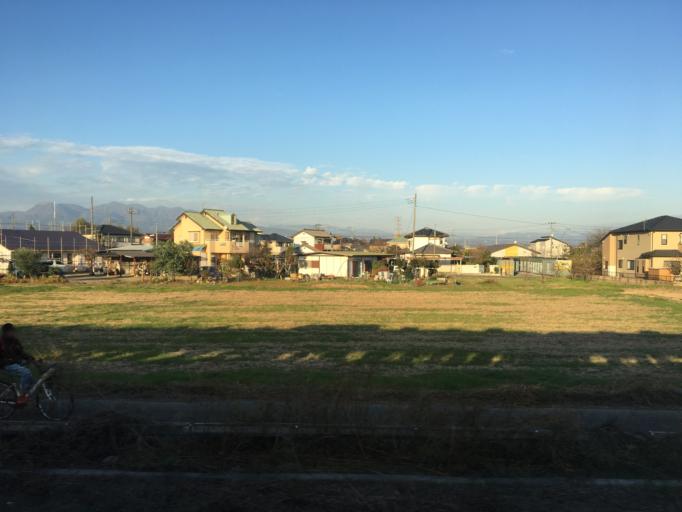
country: JP
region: Gunma
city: Maebashi-shi
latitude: 36.3651
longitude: 139.1196
